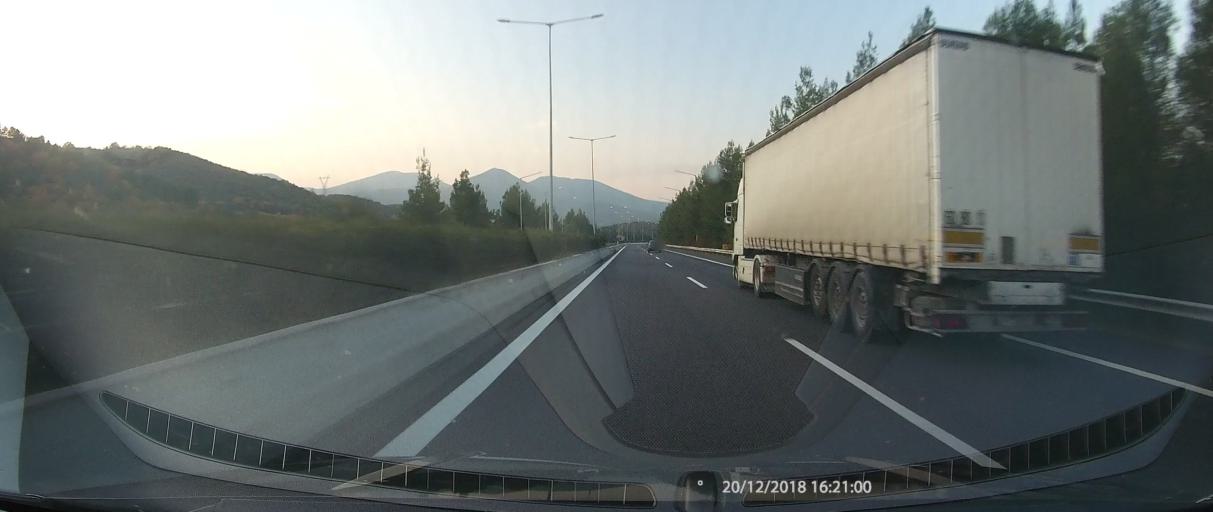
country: GR
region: Thessaly
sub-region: Nomos Magnisias
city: Pteleos
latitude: 39.0391
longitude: 22.8985
